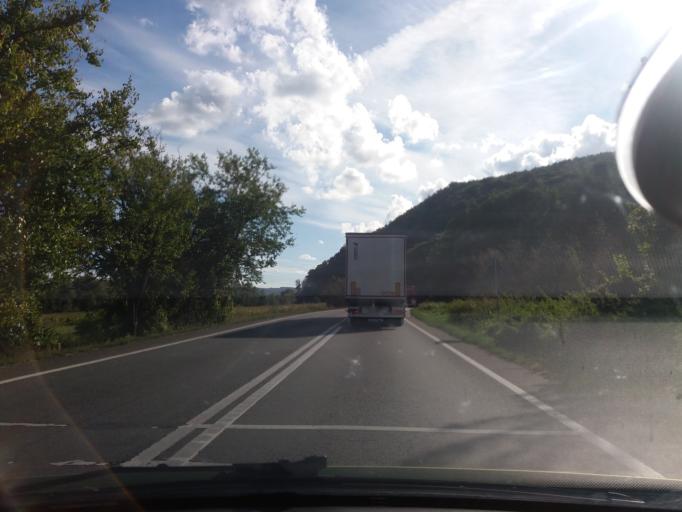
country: RO
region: Arad
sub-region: Comuna Barzava
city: Barzava
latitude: 46.1122
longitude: 21.9534
